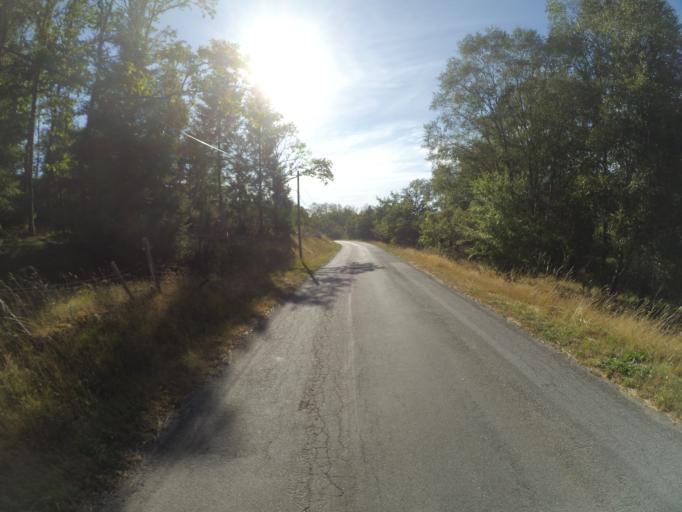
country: FR
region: Limousin
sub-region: Departement de la Correze
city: Bugeat
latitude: 45.6986
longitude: 1.9989
